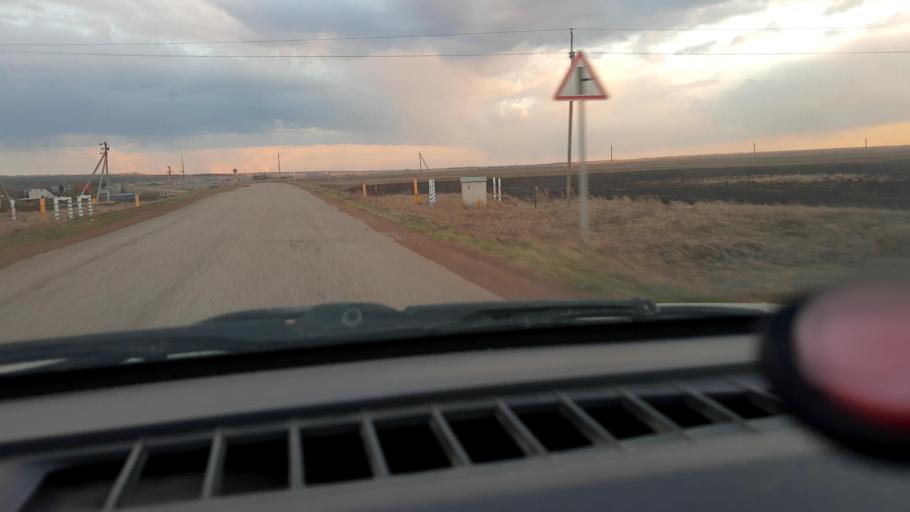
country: RU
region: Bashkortostan
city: Asanovo
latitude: 54.9404
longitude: 55.5173
